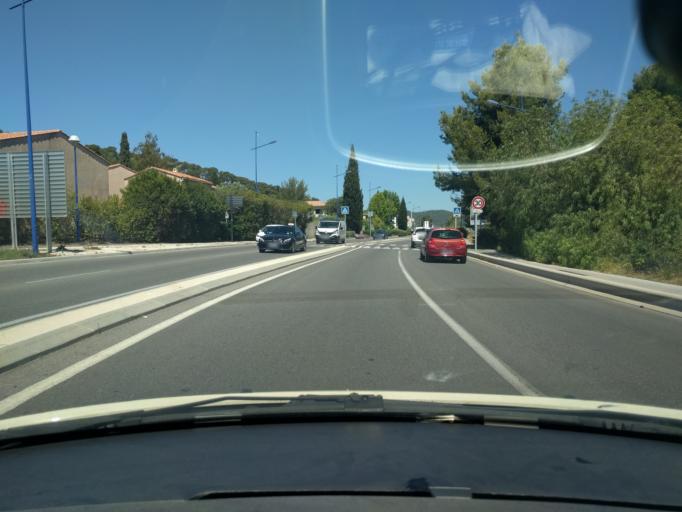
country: FR
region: Provence-Alpes-Cote d'Azur
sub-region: Departement du Var
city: Hyeres
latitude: 43.1022
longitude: 6.1296
